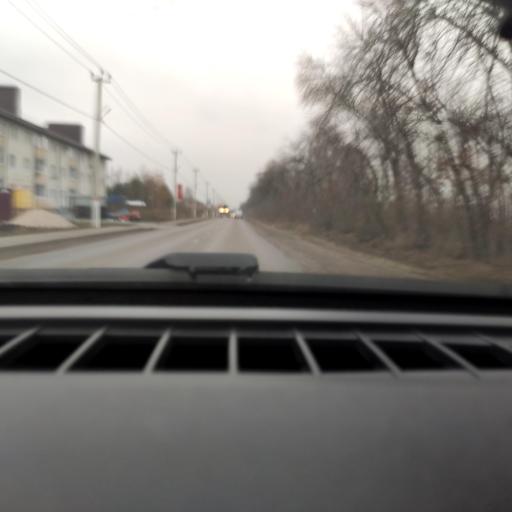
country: RU
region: Voronezj
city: Novaya Usman'
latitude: 51.6482
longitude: 39.3301
